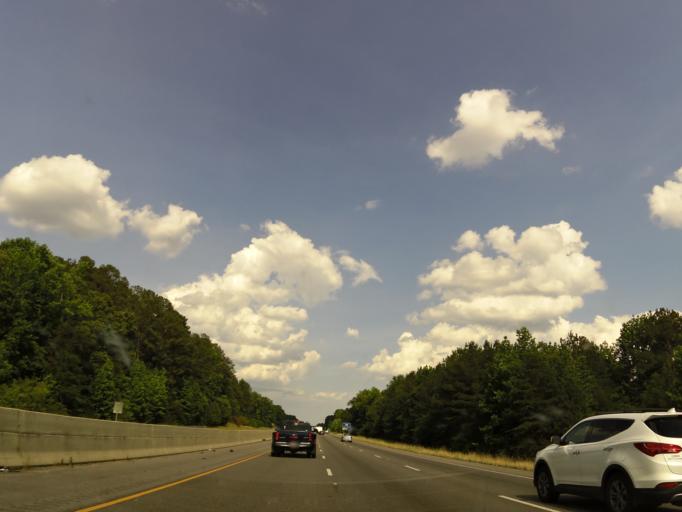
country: US
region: Alabama
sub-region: Tuscaloosa County
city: Coaling
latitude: 33.1902
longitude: -87.3130
